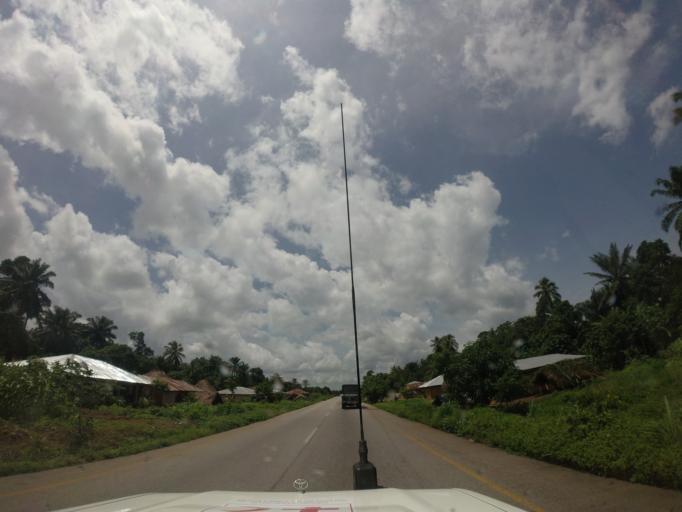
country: SL
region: Northern Province
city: Rokupr
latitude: 8.4804
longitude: -12.4515
